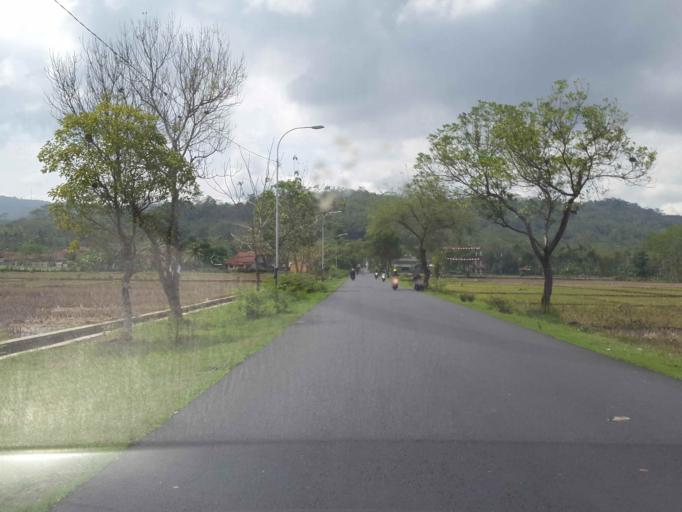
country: ID
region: Central Java
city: Banyumas
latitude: -7.5256
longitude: 109.3040
